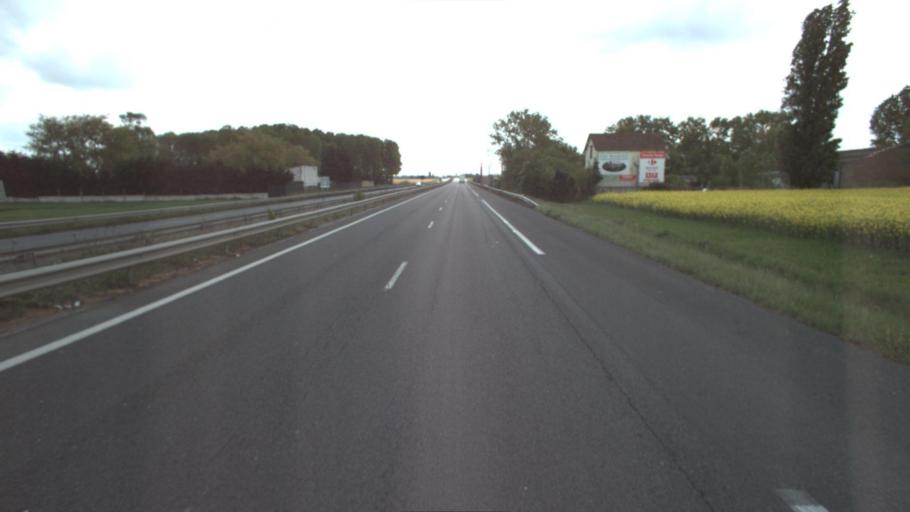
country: FR
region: Ile-de-France
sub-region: Departement de Seine-et-Marne
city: Rozay-en-Brie
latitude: 48.6900
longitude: 2.9214
